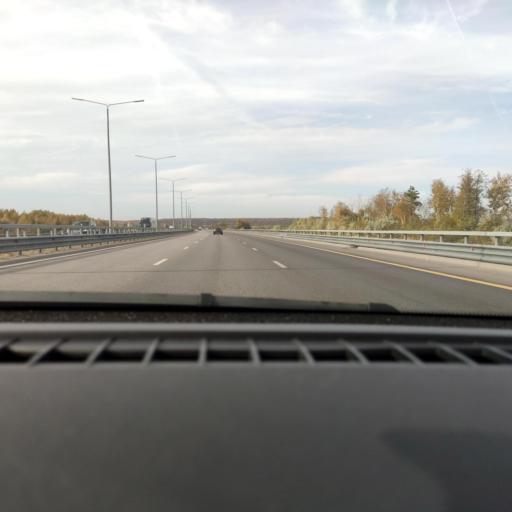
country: RU
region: Voronezj
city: Somovo
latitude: 51.7843
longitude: 39.2910
